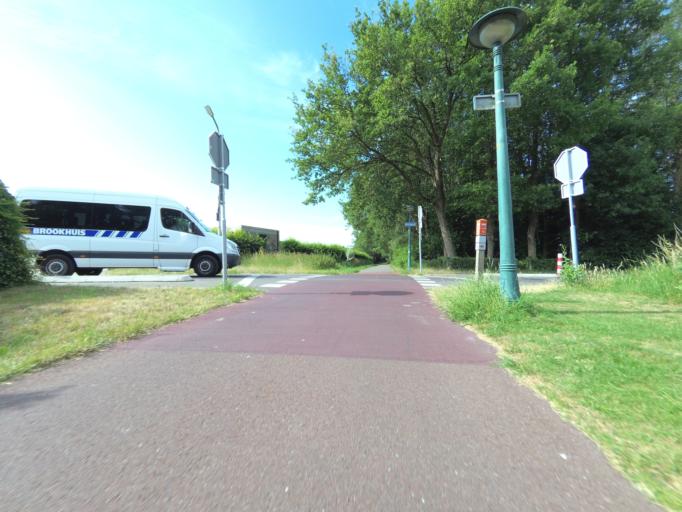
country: NL
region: Overijssel
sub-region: Gemeente Enschede
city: Enschede
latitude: 52.2426
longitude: 6.9050
